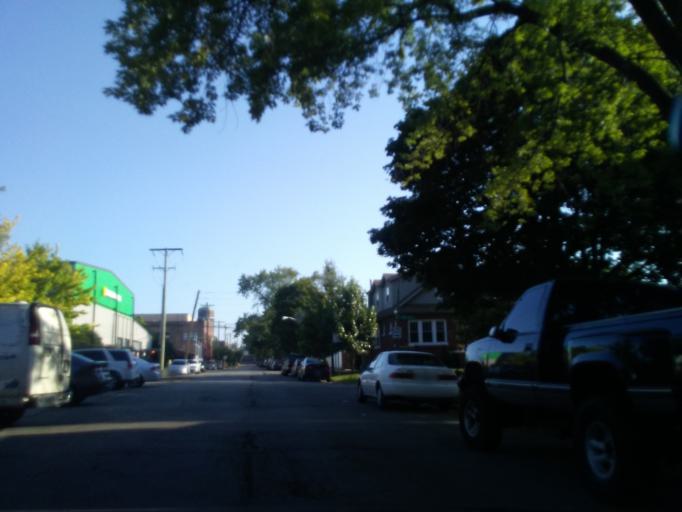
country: US
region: Illinois
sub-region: Cook County
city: Lincolnwood
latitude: 41.9360
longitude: -87.7329
